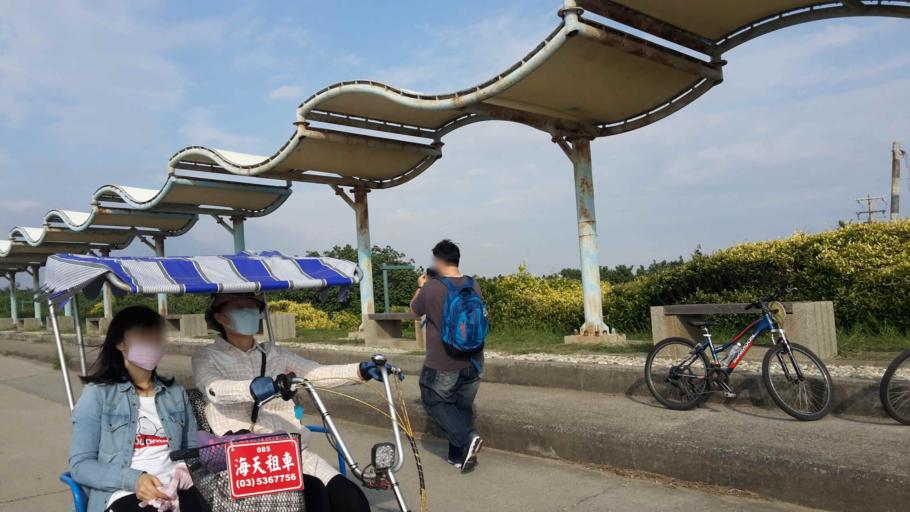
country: TW
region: Taiwan
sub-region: Hsinchu
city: Hsinchu
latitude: 24.8270
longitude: 120.9117
